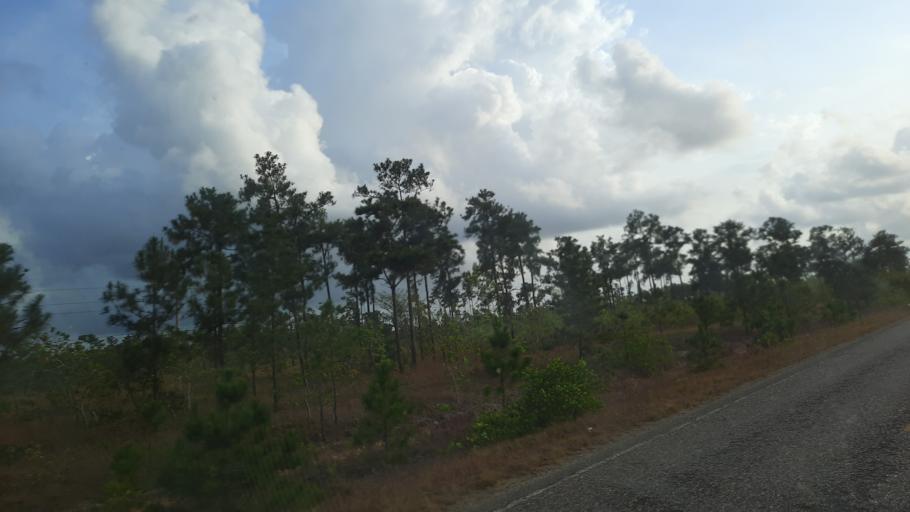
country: BZ
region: Stann Creek
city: Placencia
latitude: 16.7336
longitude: -88.3969
